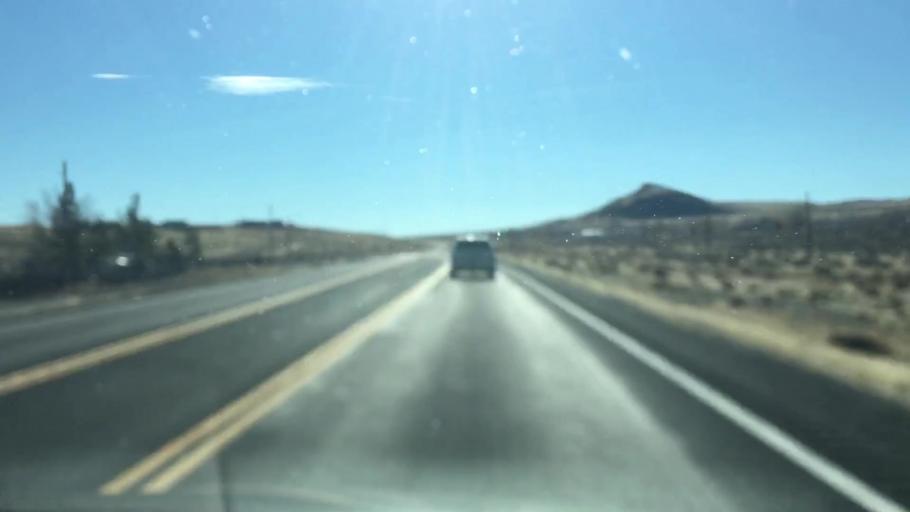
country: US
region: Nevada
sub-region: Lyon County
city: Silver Springs
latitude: 39.3480
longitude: -119.2394
